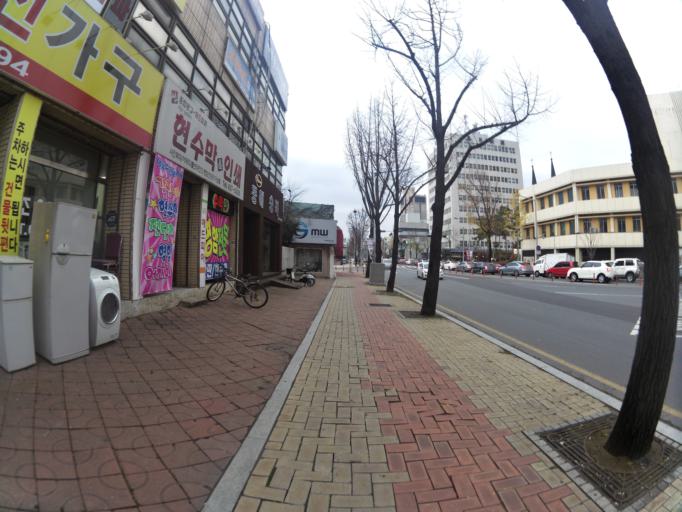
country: KR
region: Daegu
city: Daegu
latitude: 35.8672
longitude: 128.5869
